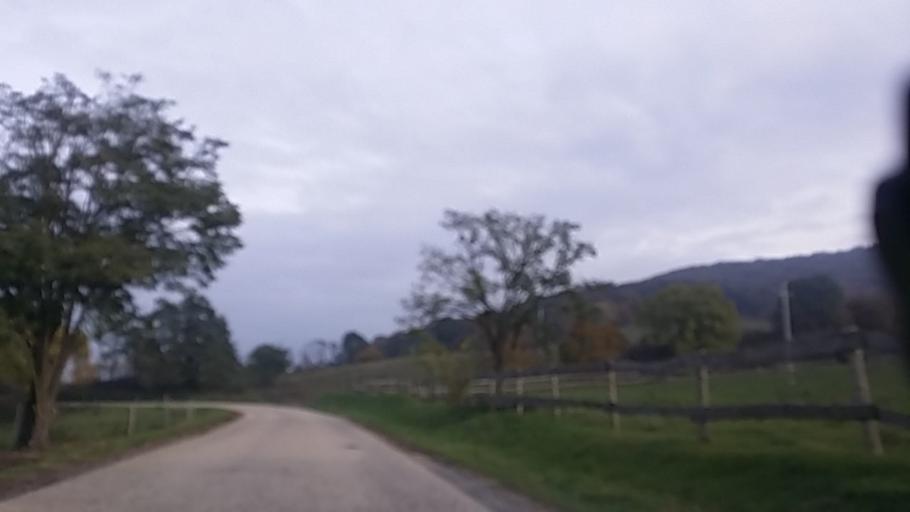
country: HU
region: Borsod-Abauj-Zemplen
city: Sajokaza
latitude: 48.2704
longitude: 20.5142
